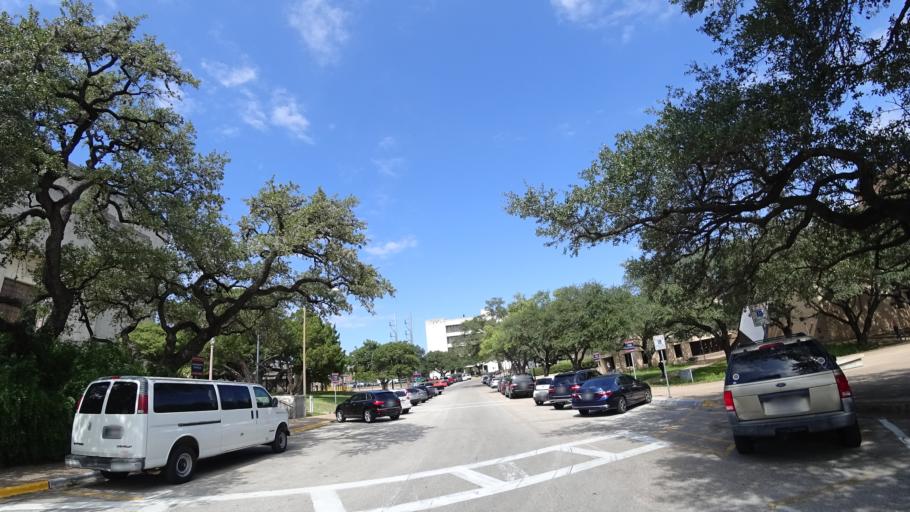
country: US
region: Texas
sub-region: Travis County
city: Austin
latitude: 30.2868
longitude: -97.7320
